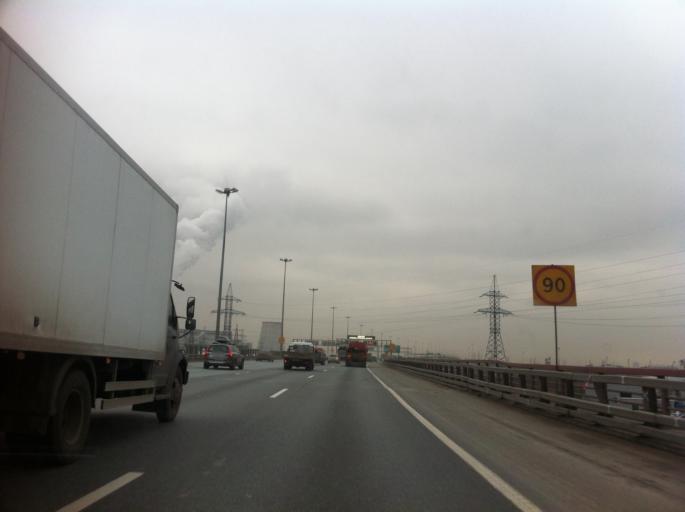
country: RU
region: St.-Petersburg
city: Obukhovo
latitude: 59.8413
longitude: 30.4550
